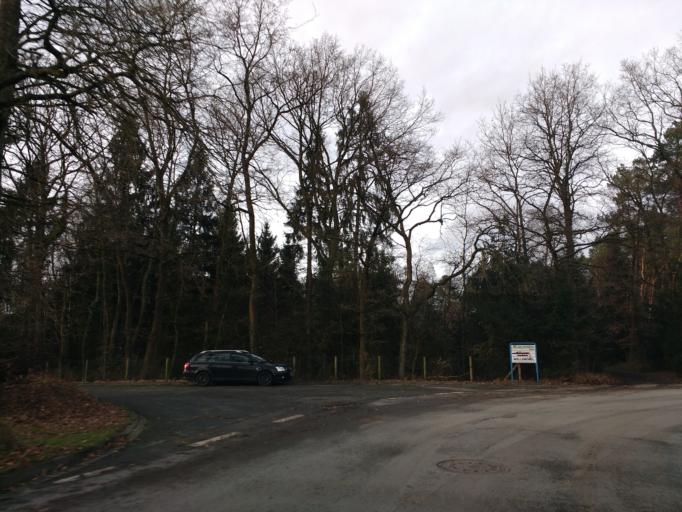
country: DE
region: North Rhine-Westphalia
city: Bad Lippspringe
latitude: 51.7790
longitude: 8.7893
